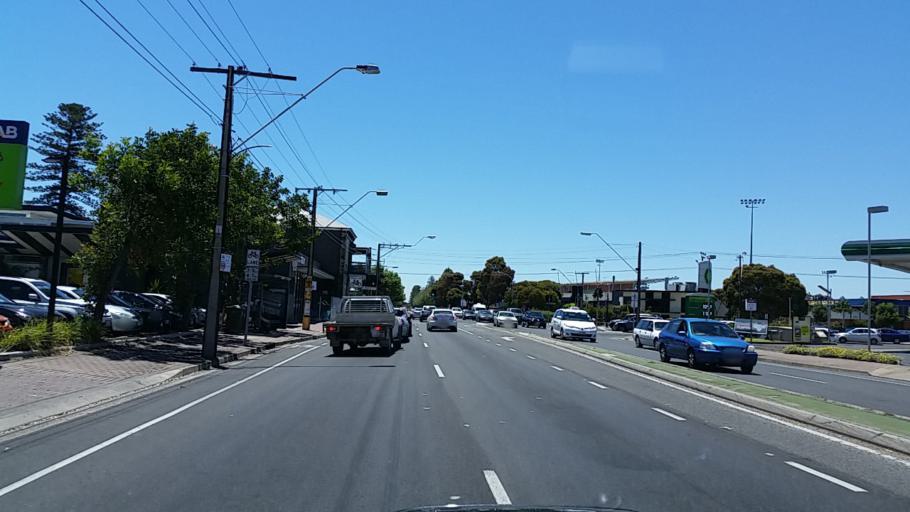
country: AU
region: South Australia
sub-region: Adelaide
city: Glenelg
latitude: -34.9858
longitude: 138.5206
